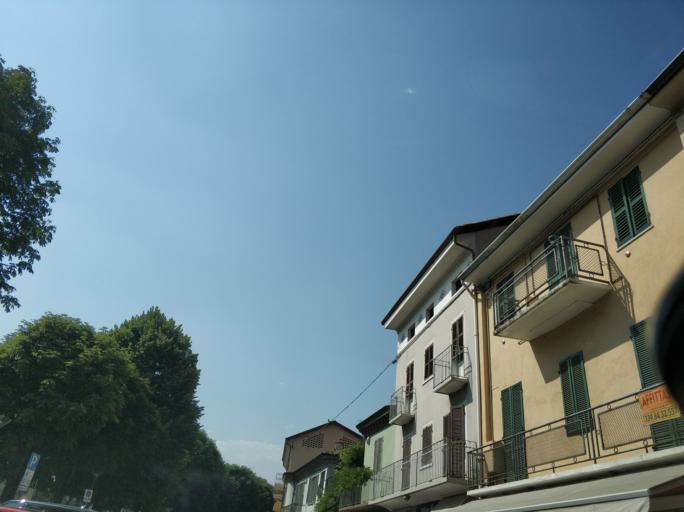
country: IT
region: Piedmont
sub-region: Provincia di Torino
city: Rivarolo Canavese
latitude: 45.3309
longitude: 7.7246
